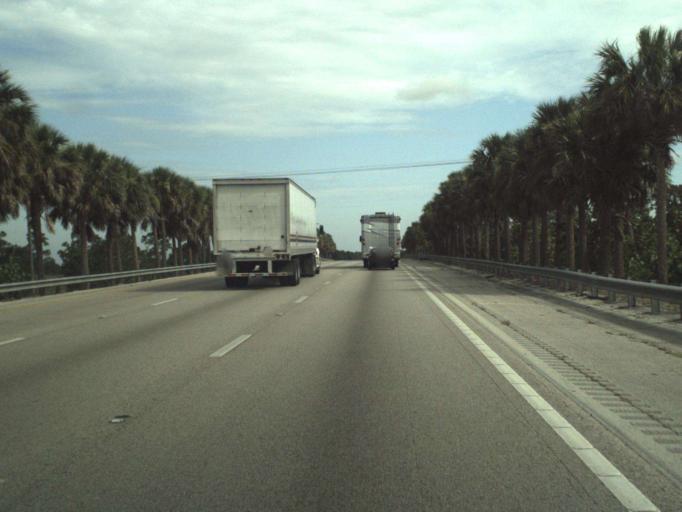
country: US
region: Florida
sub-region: Martin County
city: Palm City
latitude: 27.1603
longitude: -80.3888
